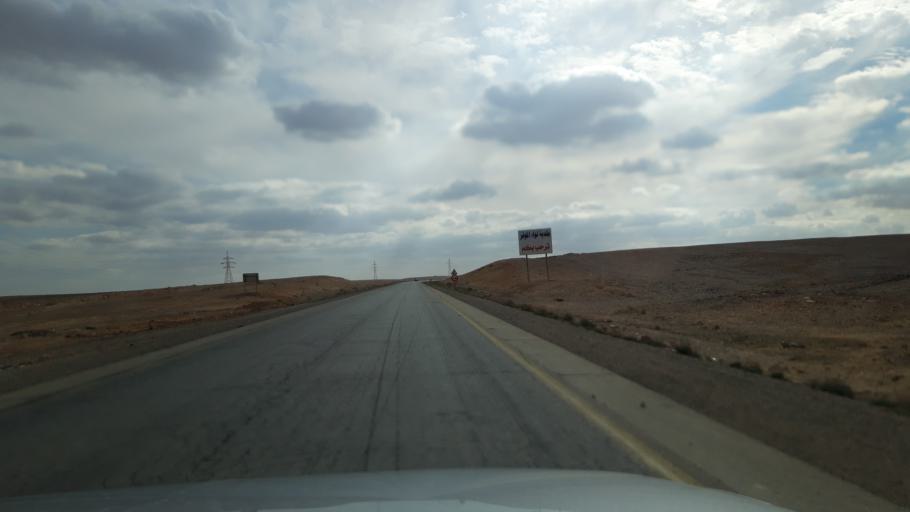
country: JO
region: Amman
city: Al Azraq ash Shamali
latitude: 31.7464
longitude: 36.5378
